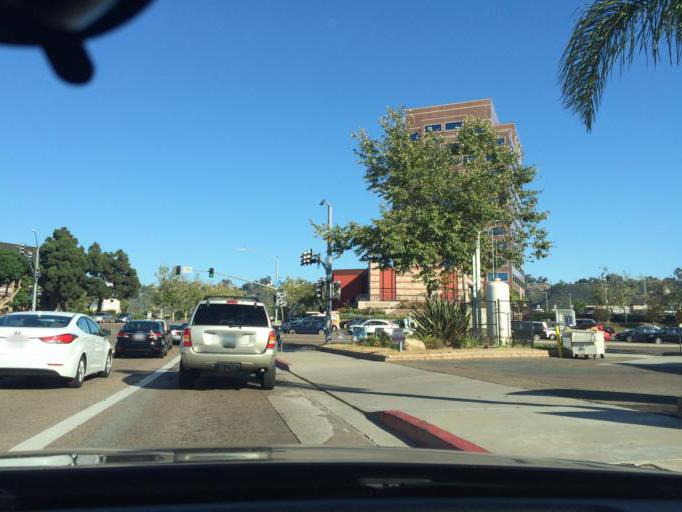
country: US
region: California
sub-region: San Diego County
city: San Diego
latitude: 32.7731
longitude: -117.1579
